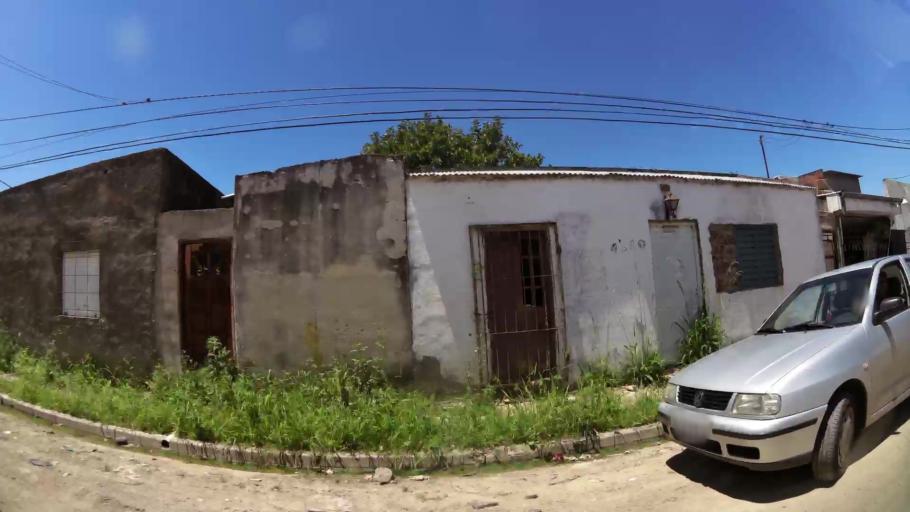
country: AR
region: Santa Fe
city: Santa Fe de la Vera Cruz
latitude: -31.6565
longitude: -60.7271
